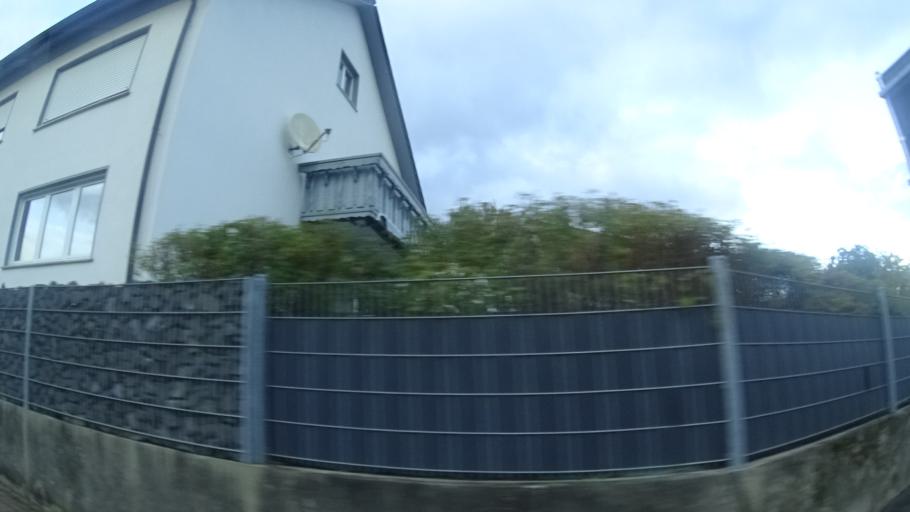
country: DE
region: Hesse
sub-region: Regierungsbezirk Kassel
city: Hosenfeld
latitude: 50.4623
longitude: 9.4769
